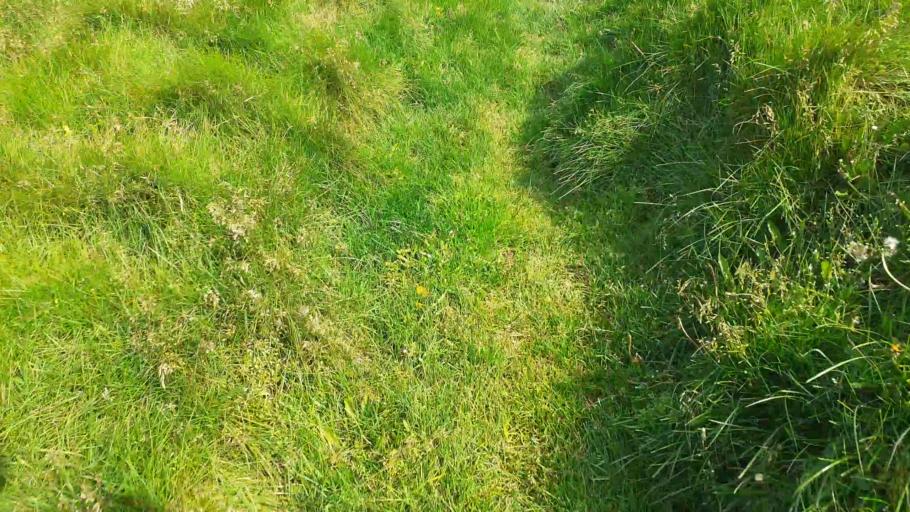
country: IS
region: Northeast
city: Dalvik
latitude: 66.5511
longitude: -17.9935
